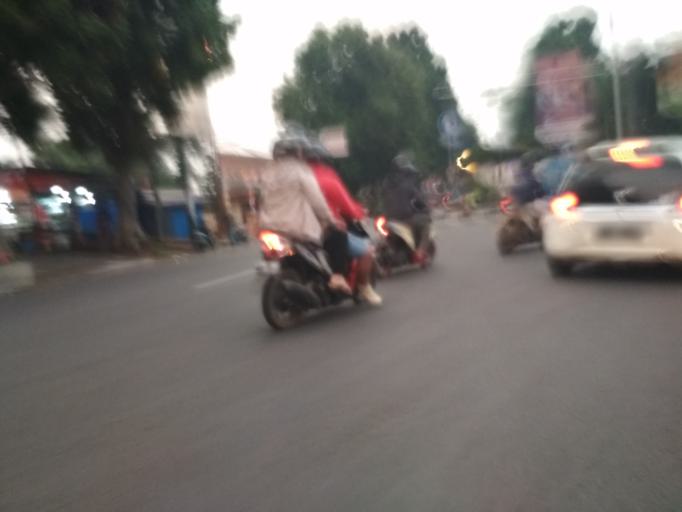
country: ID
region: West Java
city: Bogor
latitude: -6.6213
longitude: 106.8162
